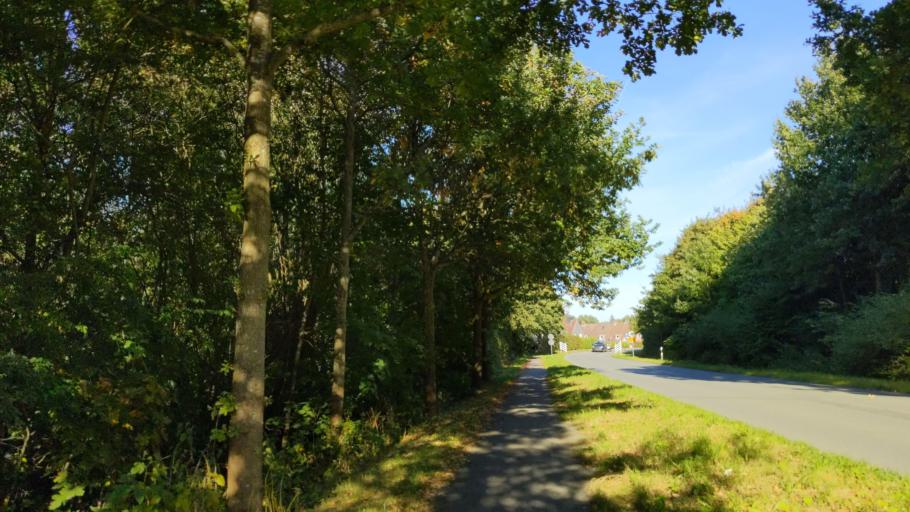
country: DE
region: Schleswig-Holstein
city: Eutin
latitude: 54.1249
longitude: 10.6024
